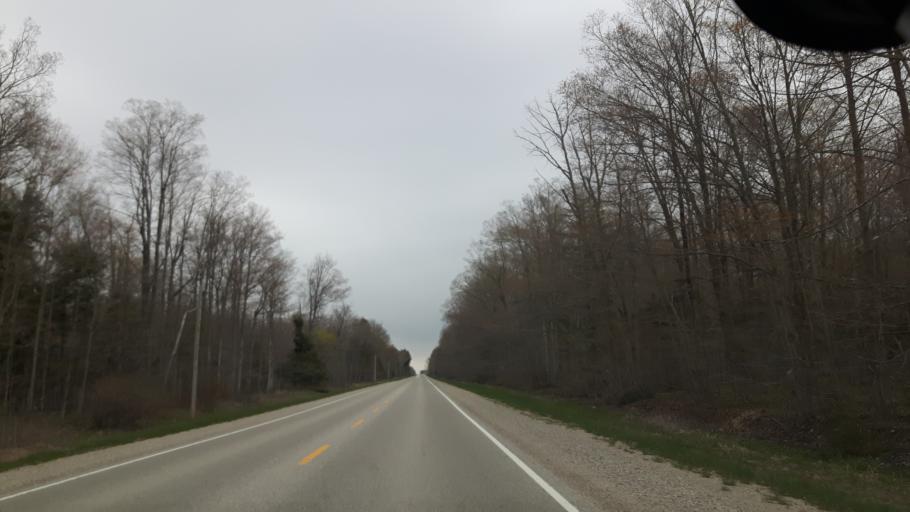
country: CA
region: Ontario
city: Bluewater
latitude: 43.5870
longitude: -81.6780
